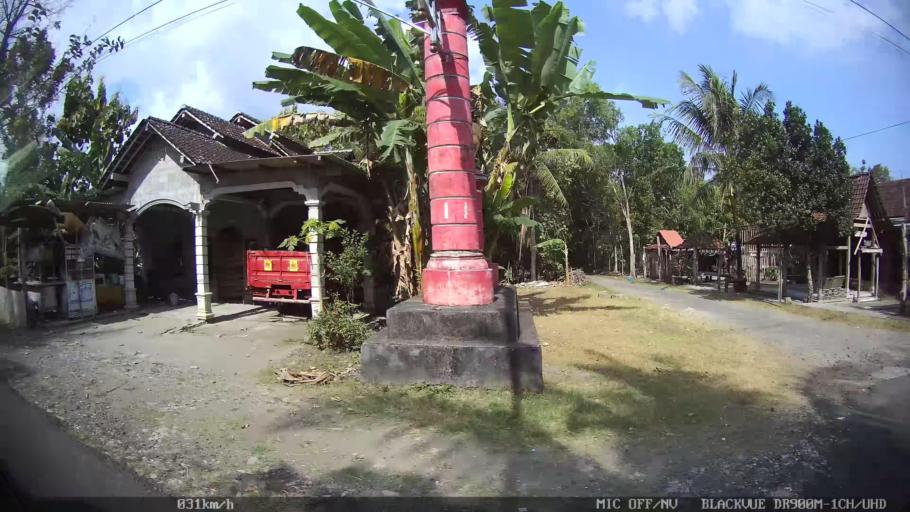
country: ID
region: Daerah Istimewa Yogyakarta
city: Kasihan
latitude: -7.8547
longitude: 110.3016
